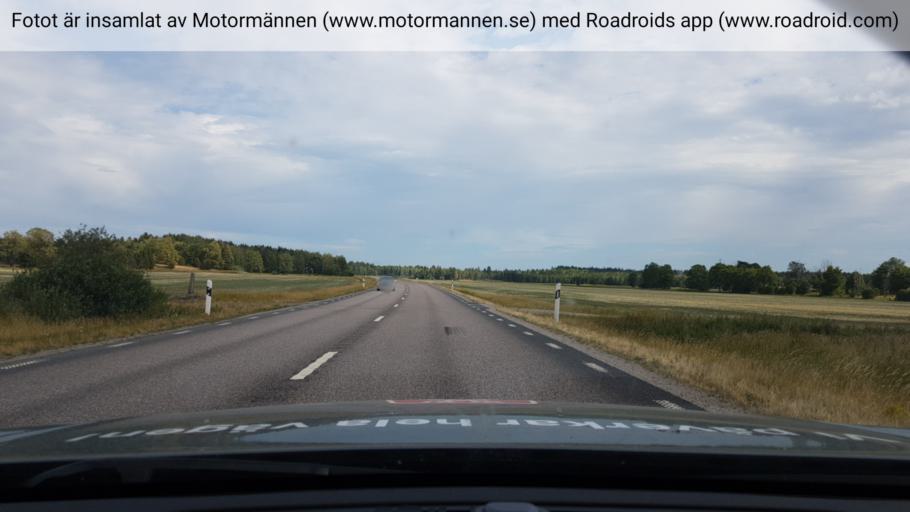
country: SE
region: Uppsala
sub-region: Enkopings Kommun
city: Orsundsbro
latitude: 59.8731
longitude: 17.2967
